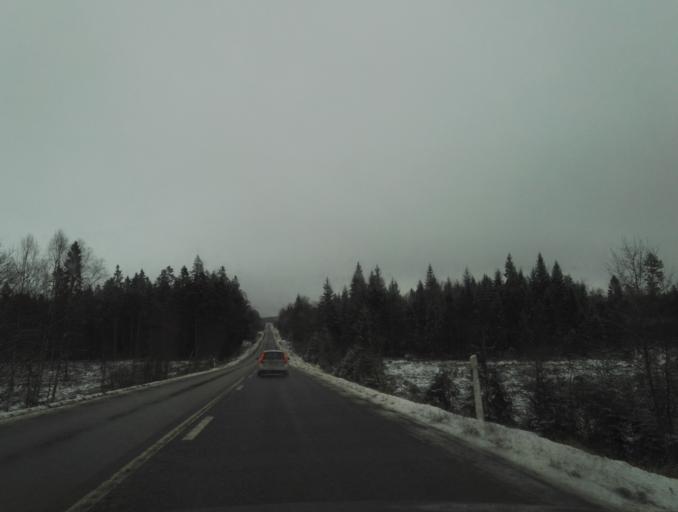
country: SE
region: Kronoberg
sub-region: Vaxjo Kommun
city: Gemla
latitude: 56.8073
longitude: 14.6603
